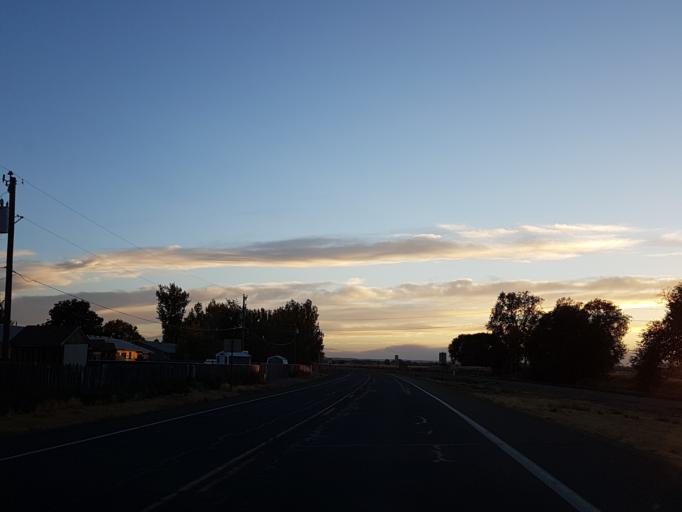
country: US
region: Oregon
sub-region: Malheur County
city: Vale
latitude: 43.9809
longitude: -117.2537
